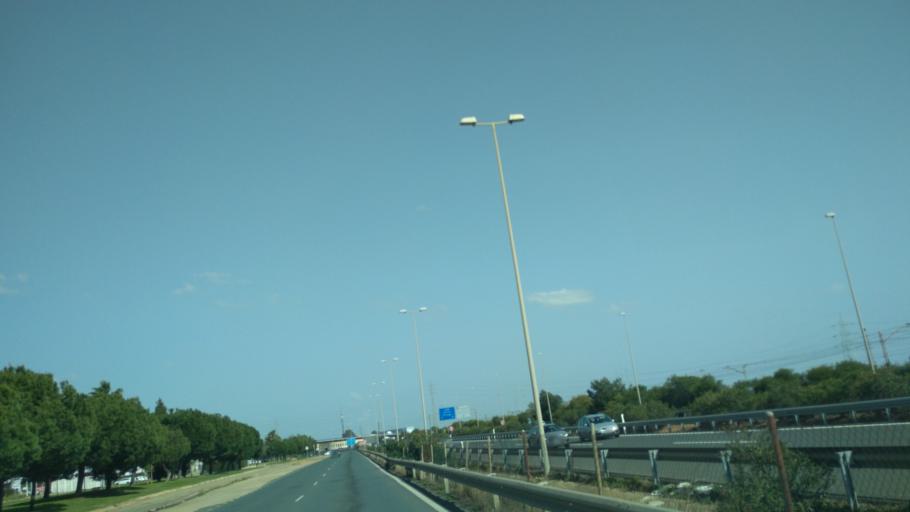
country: ES
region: Andalusia
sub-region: Provincia de Huelva
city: Huelva
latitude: 37.2563
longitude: -6.9252
